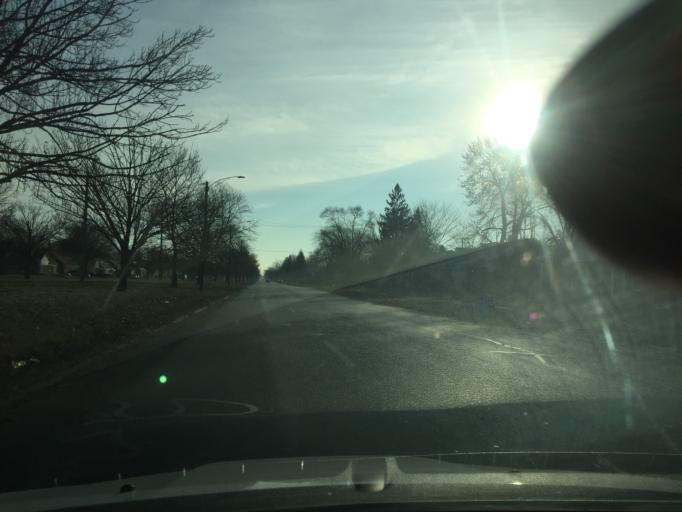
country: US
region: Michigan
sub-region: Wayne County
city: Harper Woods
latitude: 42.4341
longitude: -82.9523
